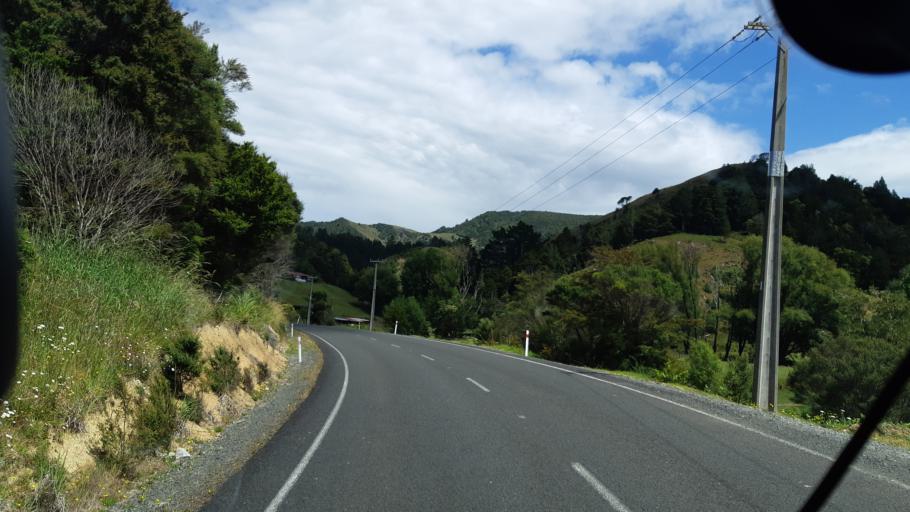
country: NZ
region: Northland
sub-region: Far North District
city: Taipa
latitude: -35.2669
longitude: 173.5023
